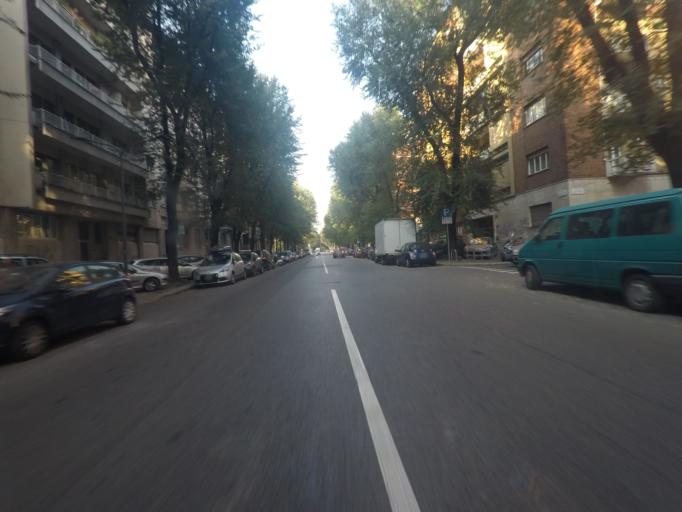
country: IT
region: Lombardy
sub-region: Citta metropolitana di Milano
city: Milano
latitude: 45.4663
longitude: 9.2302
